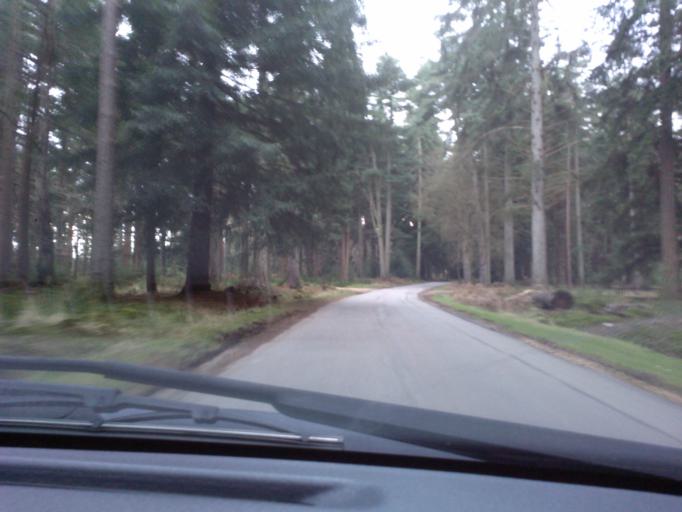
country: GB
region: England
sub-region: Hampshire
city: Lyndhurst
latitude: 50.8514
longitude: -1.6212
